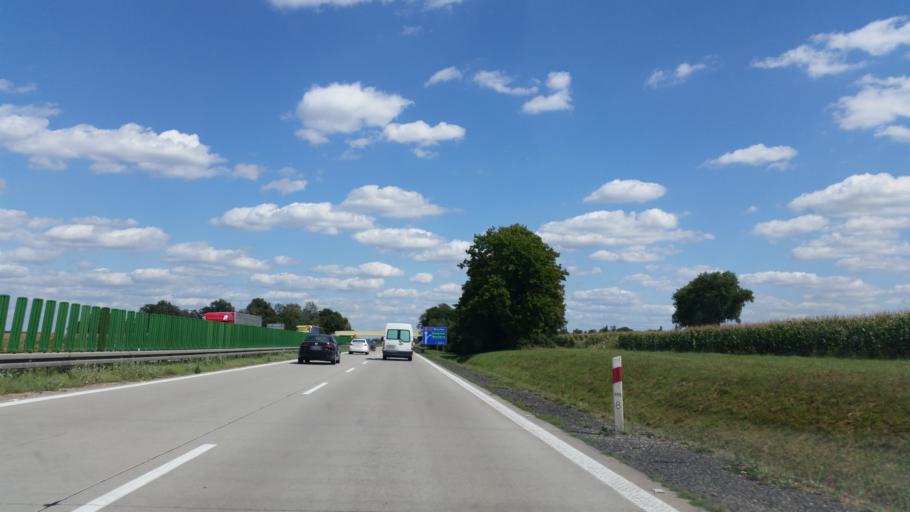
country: PL
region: Lower Silesian Voivodeship
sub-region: Powiat wroclawski
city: Smolec
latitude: 51.0354
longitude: 16.8668
